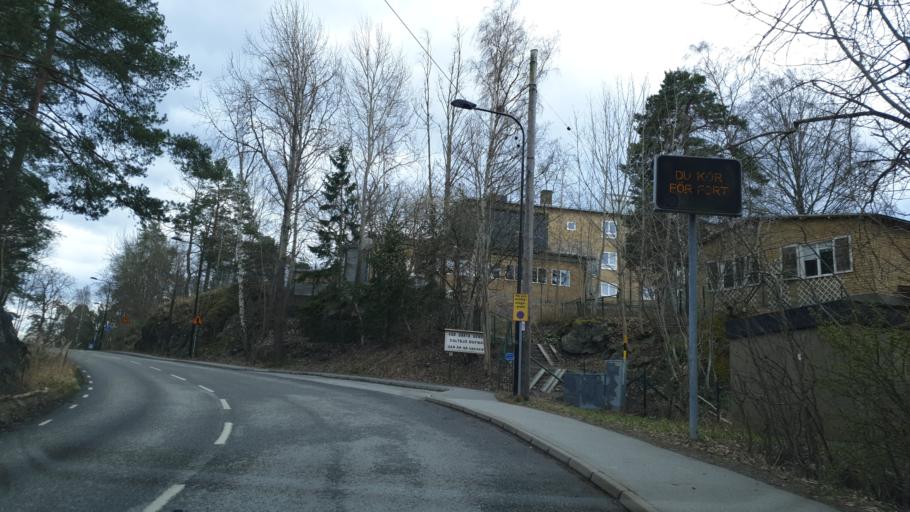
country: SE
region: Stockholm
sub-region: Nacka Kommun
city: Nacka
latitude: 59.3067
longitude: 18.2001
